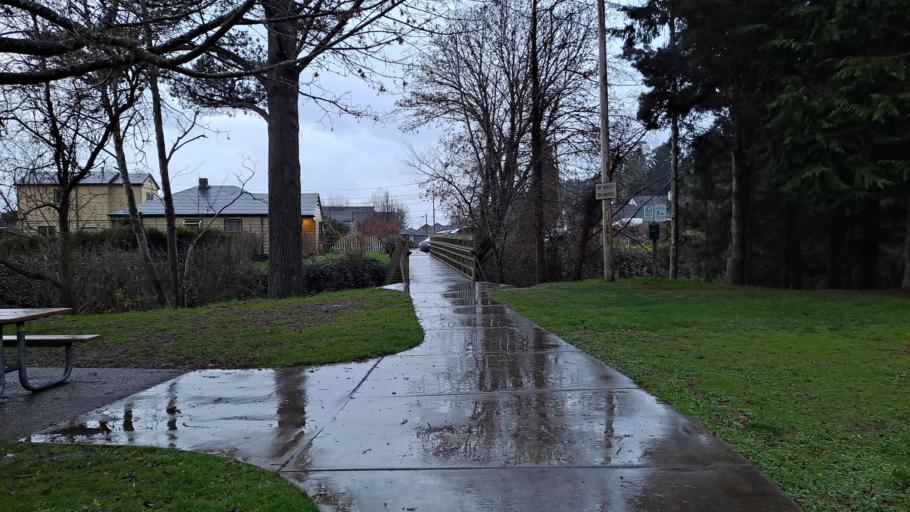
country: US
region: California
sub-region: Humboldt County
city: Fortuna
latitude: 40.5997
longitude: -124.1502
